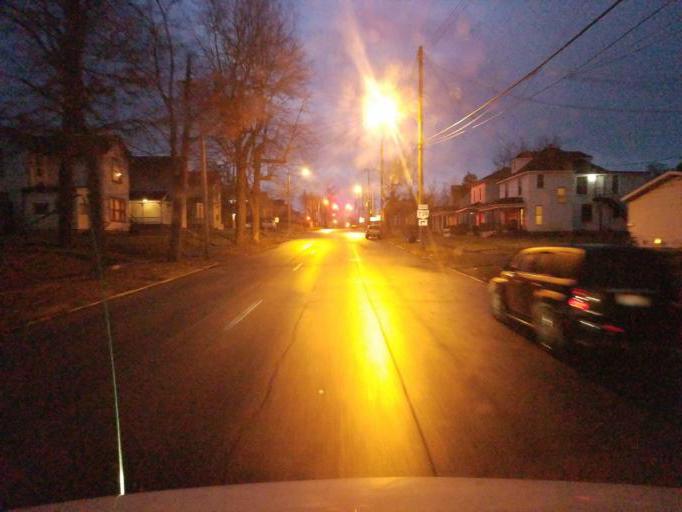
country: US
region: Ohio
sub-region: Marion County
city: Marion
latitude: 40.5835
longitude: -83.1301
